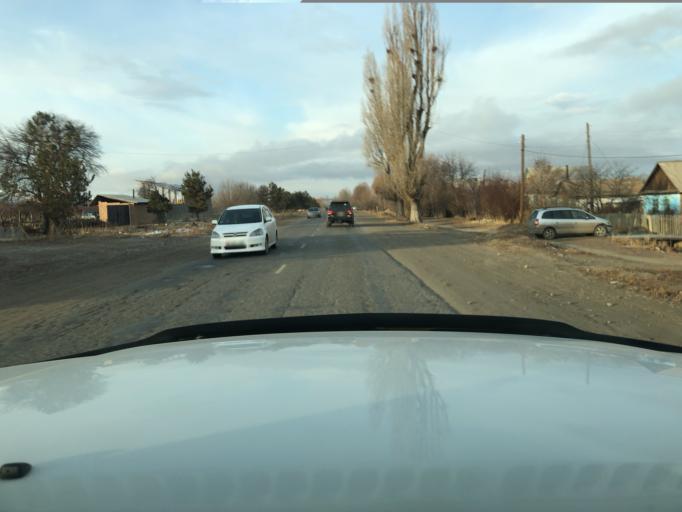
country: KG
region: Ysyk-Koel
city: Karakol
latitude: 42.4823
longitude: 78.3597
